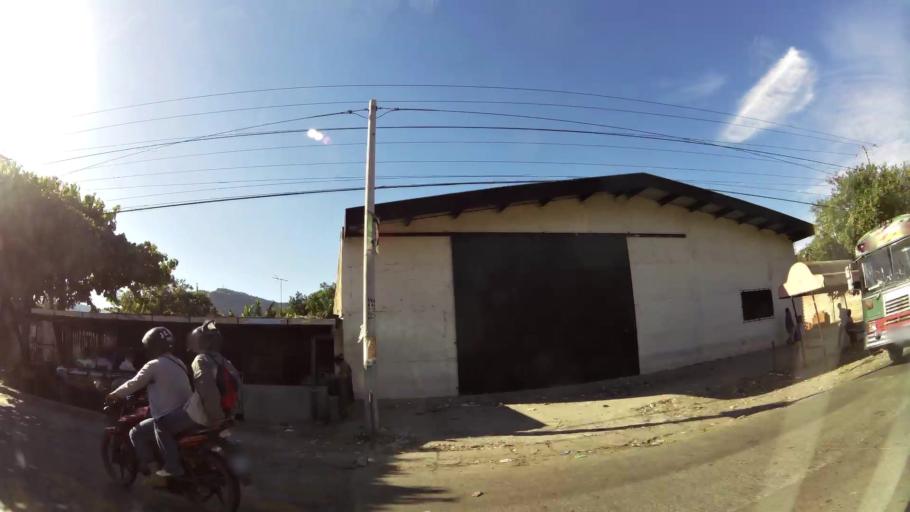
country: SV
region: Santa Ana
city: Santa Ana
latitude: 14.0171
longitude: -89.5374
